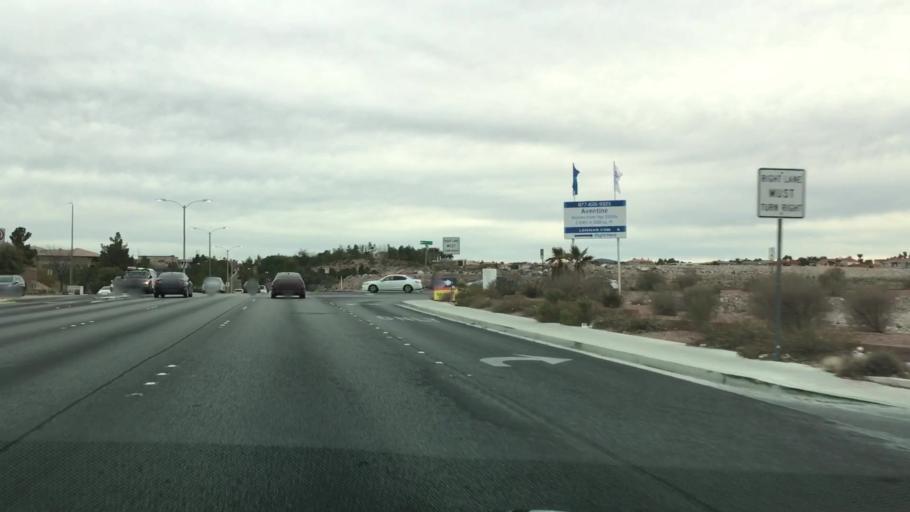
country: US
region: Nevada
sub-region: Clark County
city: Whitney
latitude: 35.9868
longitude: -115.0890
